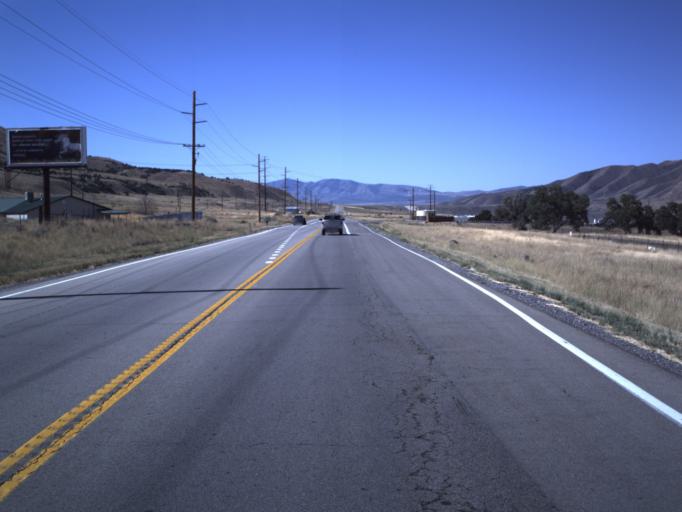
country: US
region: Utah
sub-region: Tooele County
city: Tooele
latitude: 40.4994
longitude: -112.3255
